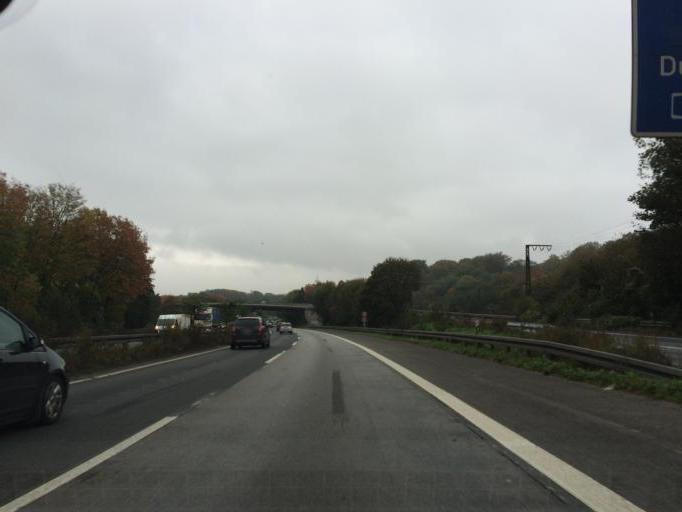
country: DE
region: North Rhine-Westphalia
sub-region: Regierungsbezirk Dusseldorf
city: Duisburg
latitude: 51.4430
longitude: 6.8009
